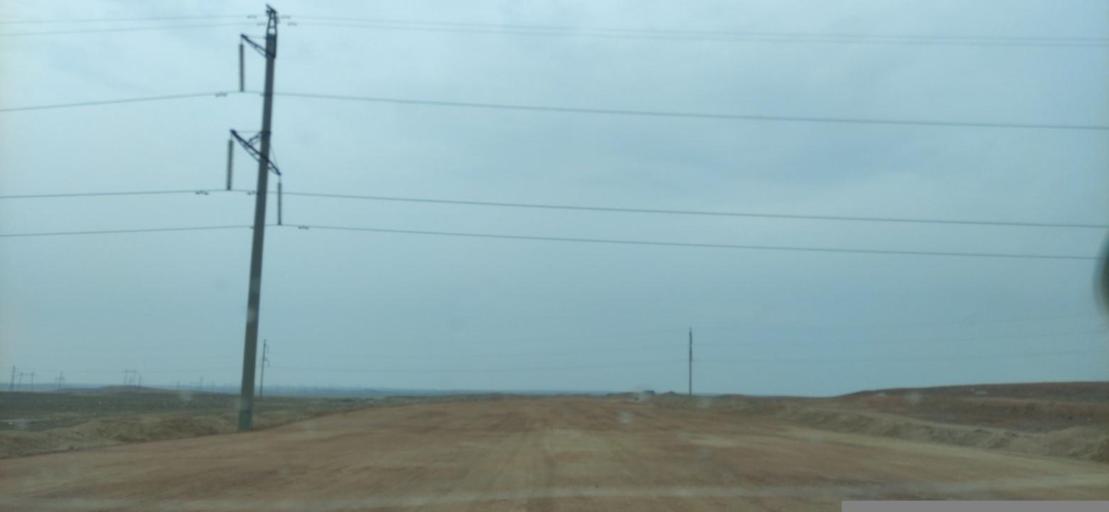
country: KZ
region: Qaraghandy
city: Saryshaghan
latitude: 46.1200
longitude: 73.5949
